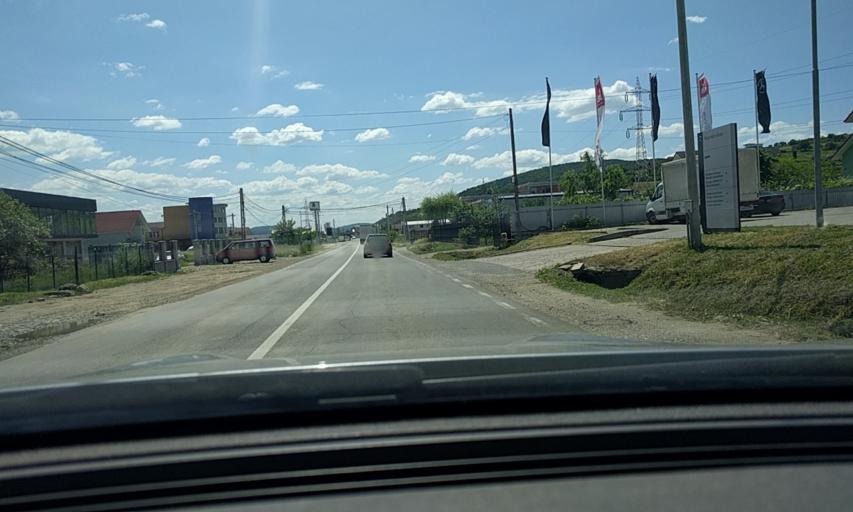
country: RO
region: Bistrita-Nasaud
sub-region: Municipiul Bistrita
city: Viisoara
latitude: 47.1235
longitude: 24.4625
